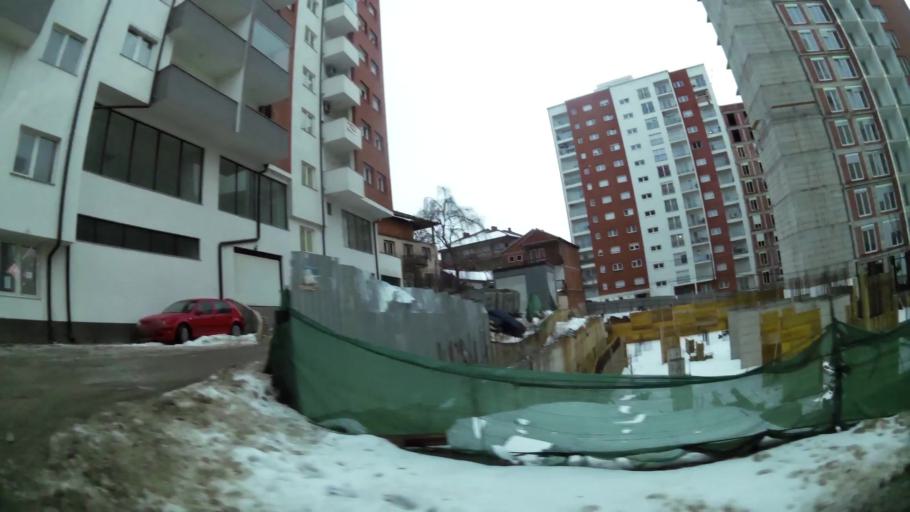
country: XK
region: Pristina
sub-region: Komuna e Prishtines
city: Pristina
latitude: 42.6587
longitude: 21.1715
